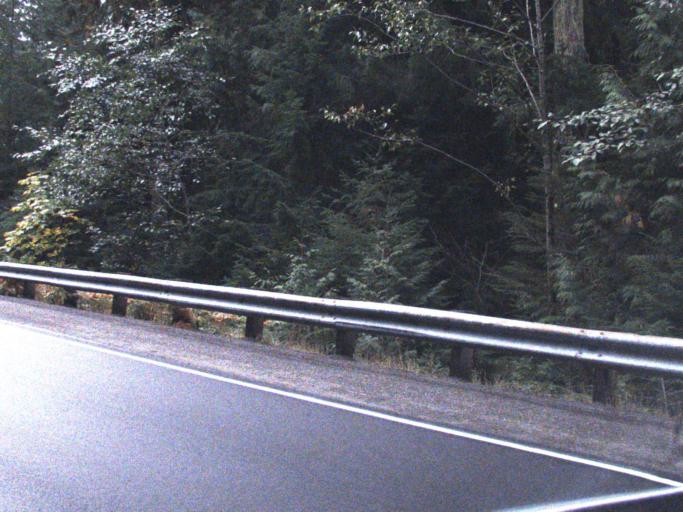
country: US
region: Washington
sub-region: Pierce County
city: Buckley
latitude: 46.6846
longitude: -121.5491
